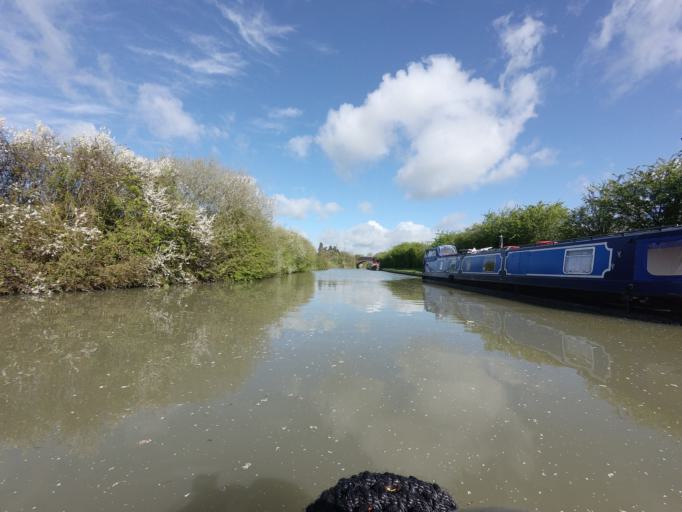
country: GB
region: England
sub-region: Northamptonshire
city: Blisworth
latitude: 52.1807
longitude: -0.9417
